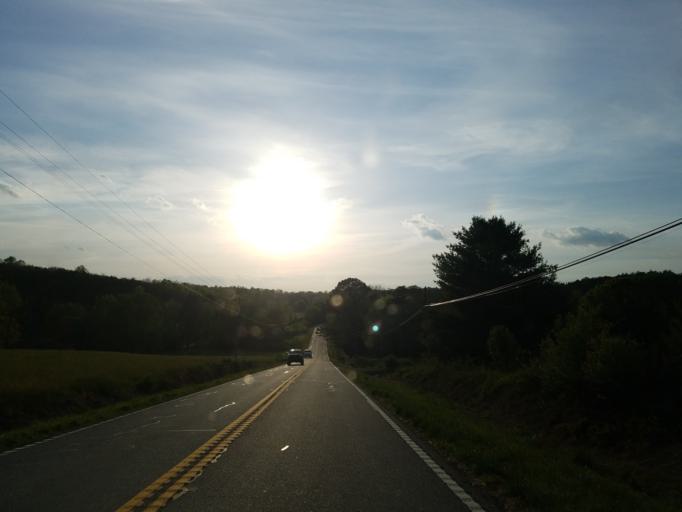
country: US
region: Georgia
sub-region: Fannin County
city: Blue Ridge
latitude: 34.8453
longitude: -84.2115
